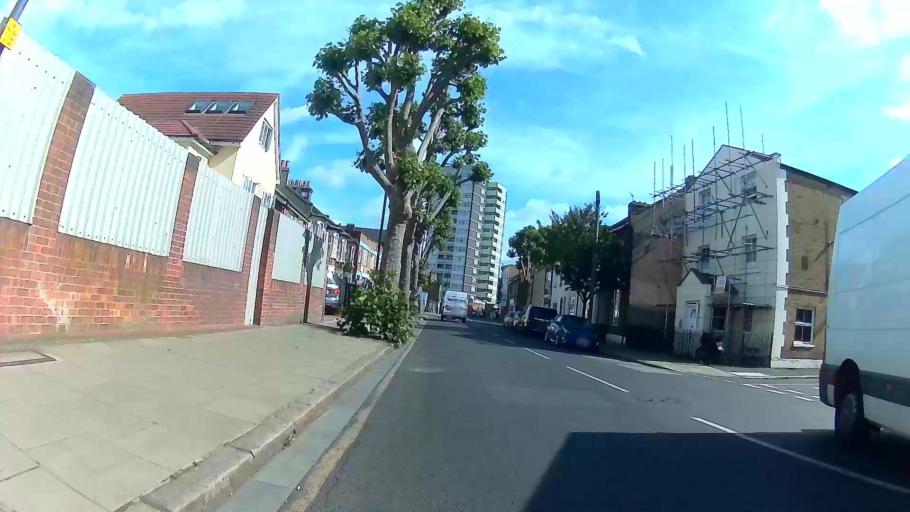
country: GB
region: England
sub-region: Greater London
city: East Ham
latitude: 51.5283
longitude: 0.0241
